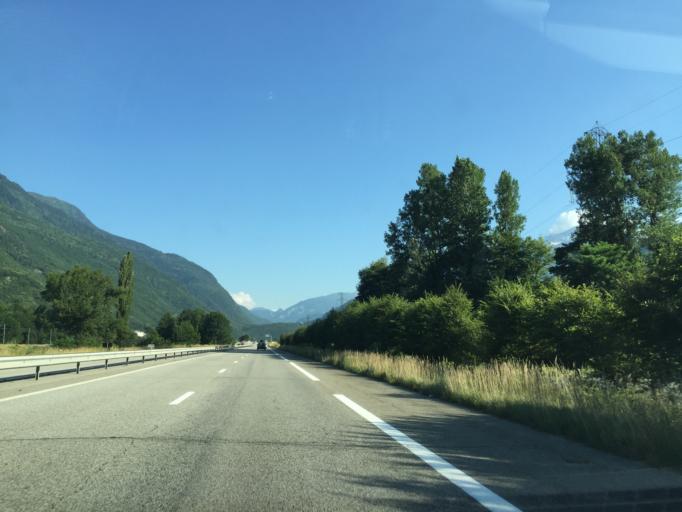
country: FR
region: Rhone-Alpes
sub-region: Departement de la Savoie
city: La Bathie
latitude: 45.6357
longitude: 6.4418
